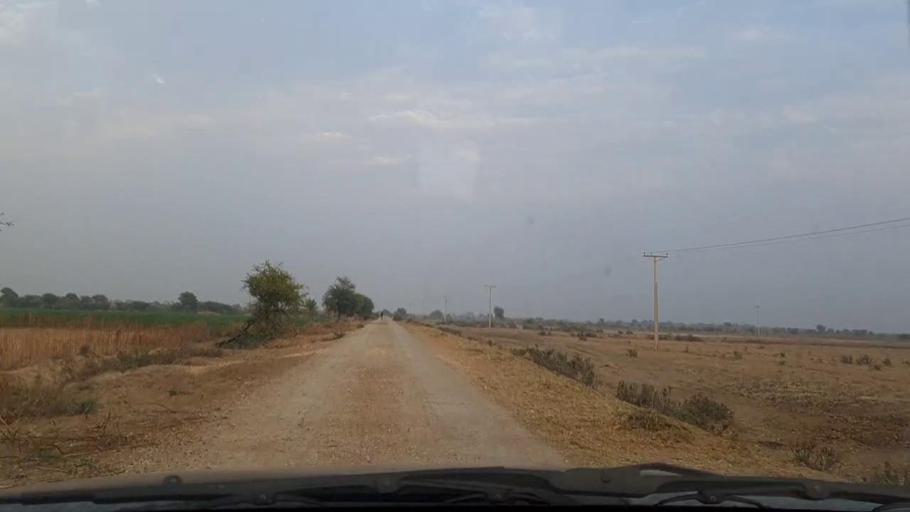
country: PK
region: Sindh
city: Dhoro Naro
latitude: 25.5932
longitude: 69.4831
